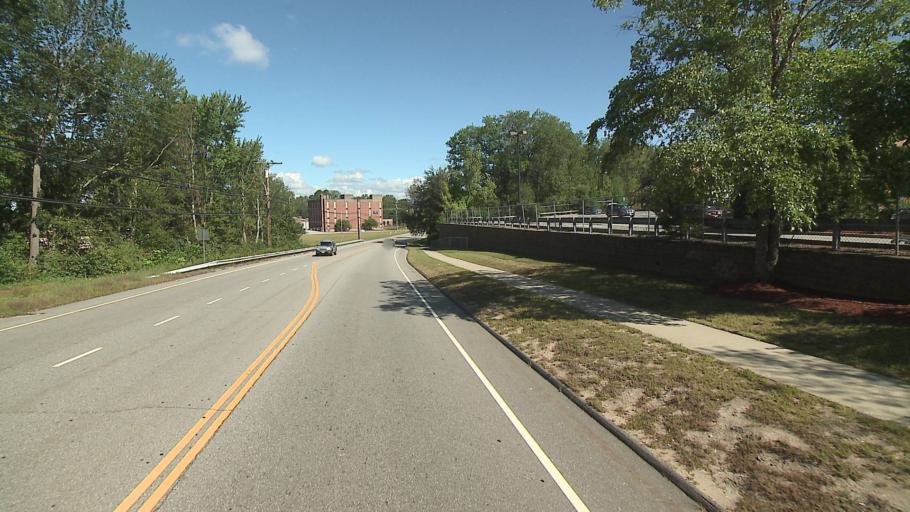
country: US
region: Connecticut
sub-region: Windham County
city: Danielson
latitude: 41.7927
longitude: -71.8849
